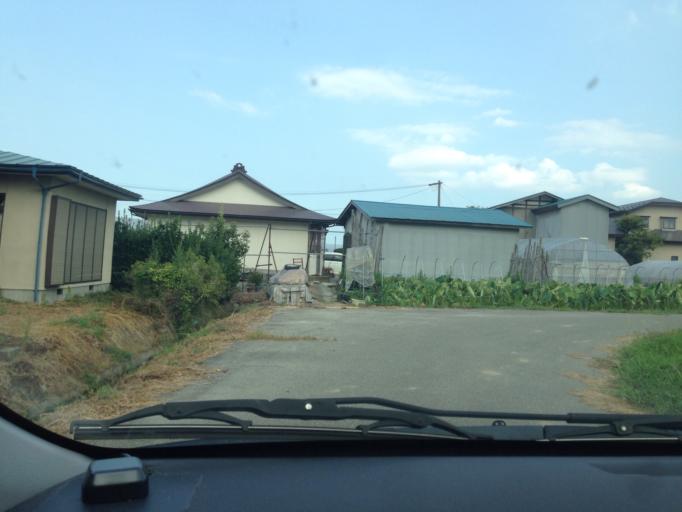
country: JP
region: Fukushima
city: Kitakata
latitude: 37.5176
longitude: 139.8585
